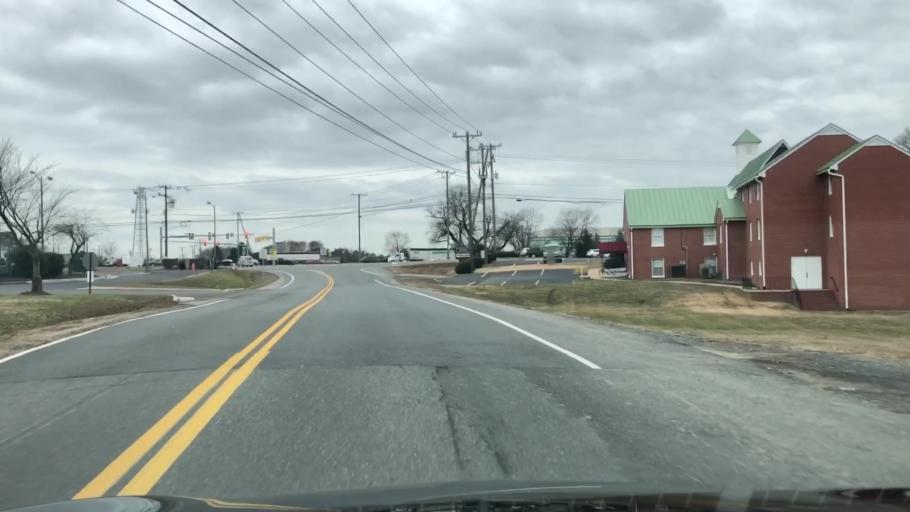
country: US
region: Virginia
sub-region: Stafford County
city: Falmouth
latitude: 38.3625
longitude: -77.5185
